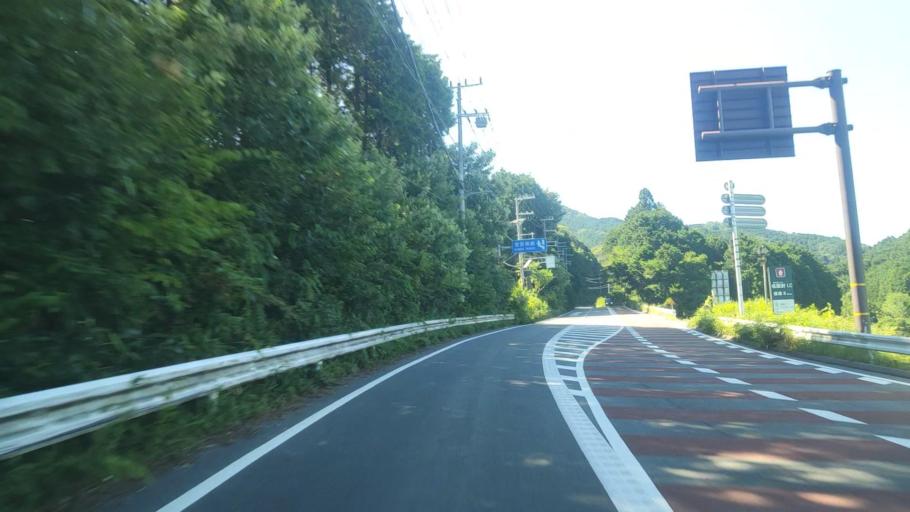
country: JP
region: Nara
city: Haibara-akanedai
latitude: 34.5486
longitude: 135.9601
